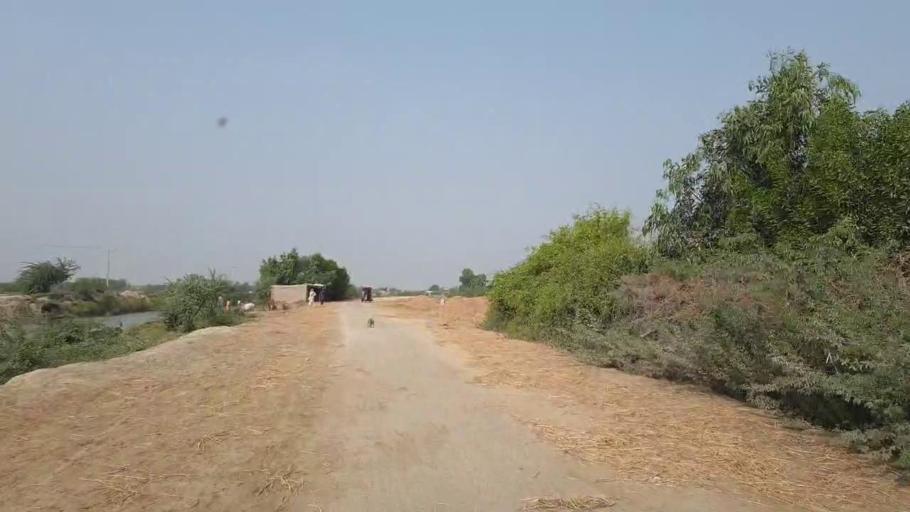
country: PK
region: Sindh
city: Kario
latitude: 24.9193
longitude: 68.6014
